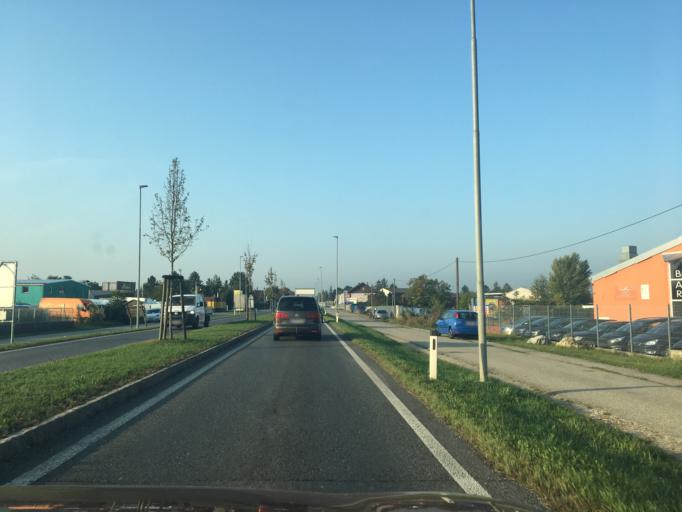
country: AT
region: Lower Austria
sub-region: Politischer Bezirk Wien-Umgebung
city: Gerasdorf bei Wien
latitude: 48.3222
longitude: 16.4430
